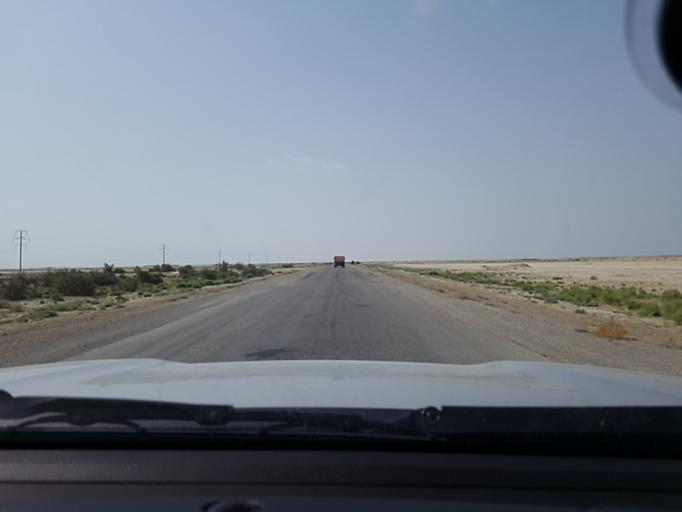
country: TM
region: Balkan
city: Gumdag
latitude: 38.9201
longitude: 54.5911
